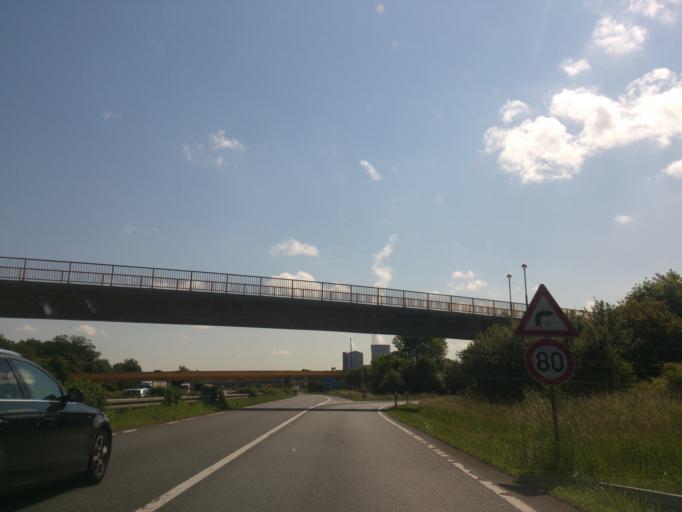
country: DE
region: Lower Saxony
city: Garbsen-Mitte
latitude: 52.4206
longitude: 9.6267
